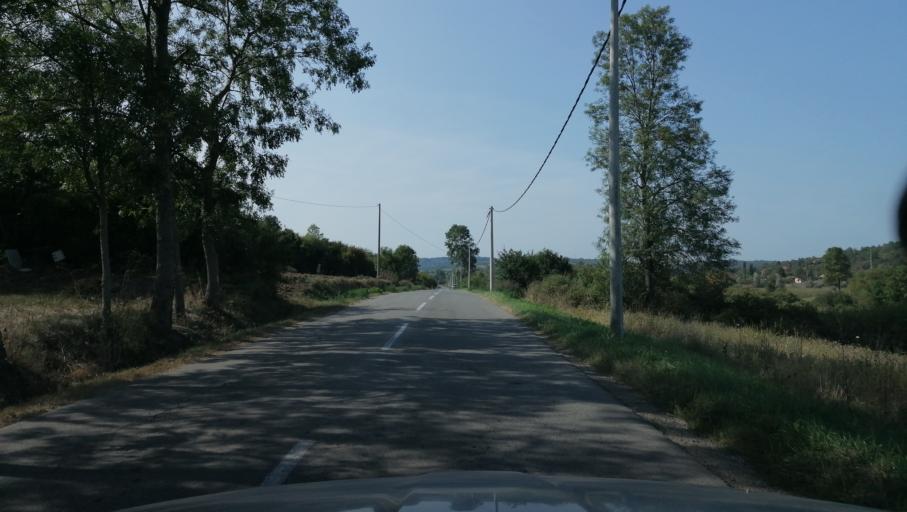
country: RS
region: Central Serbia
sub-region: Belgrade
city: Sopot
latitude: 44.5694
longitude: 20.6234
